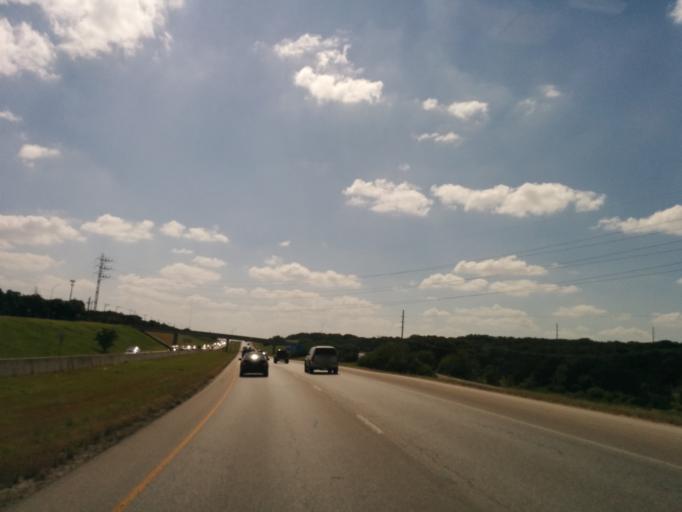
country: US
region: Texas
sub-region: Bexar County
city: Live Oak
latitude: 29.6030
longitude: -98.3627
